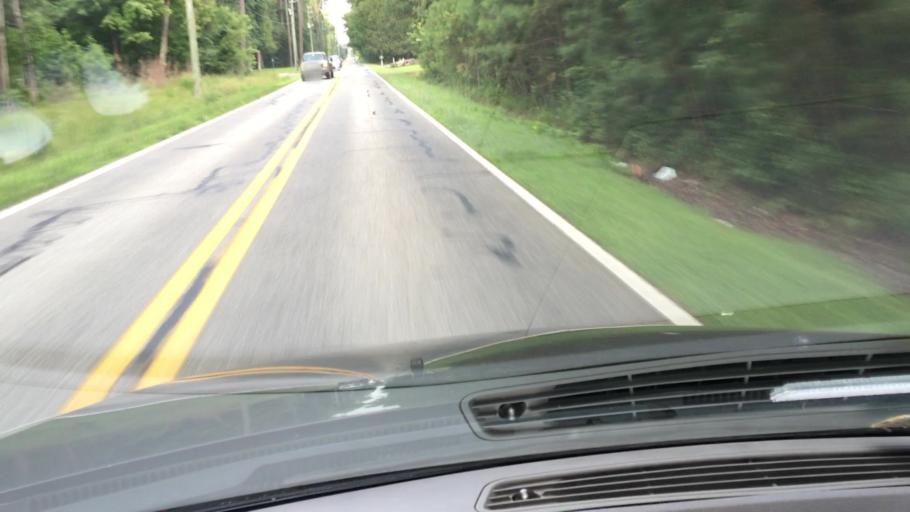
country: US
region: Delaware
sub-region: Sussex County
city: Ocean View
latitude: 38.5149
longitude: -75.0898
